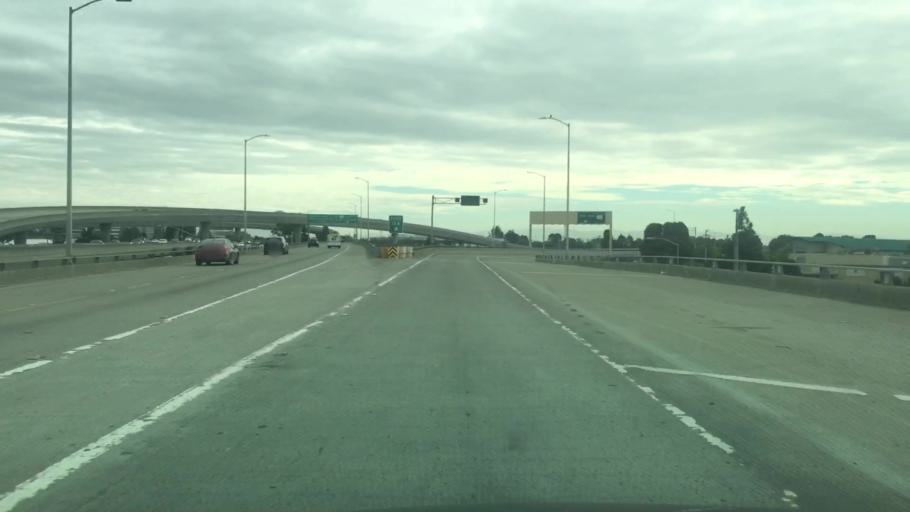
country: US
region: California
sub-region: San Mateo County
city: San Mateo
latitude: 37.5525
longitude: -122.2998
